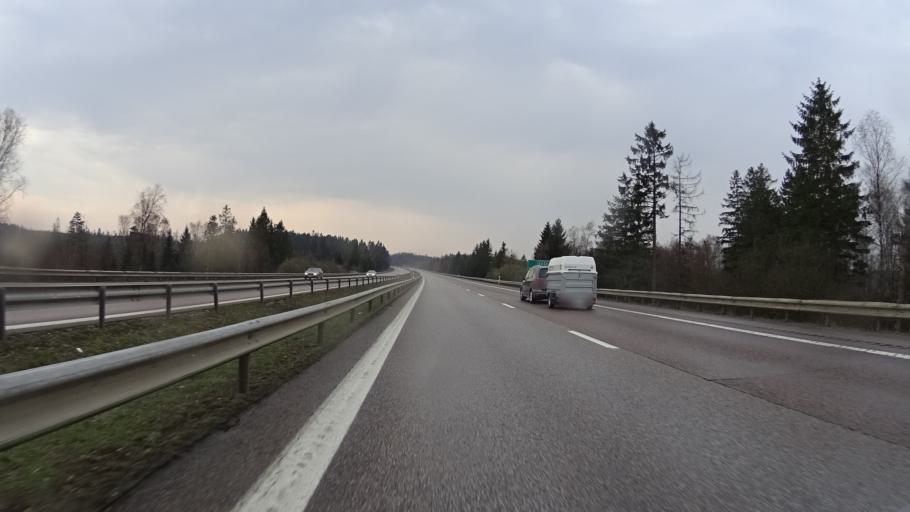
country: SE
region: Skane
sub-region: Bastads Kommun
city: Bastad
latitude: 56.3824
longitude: 12.9359
